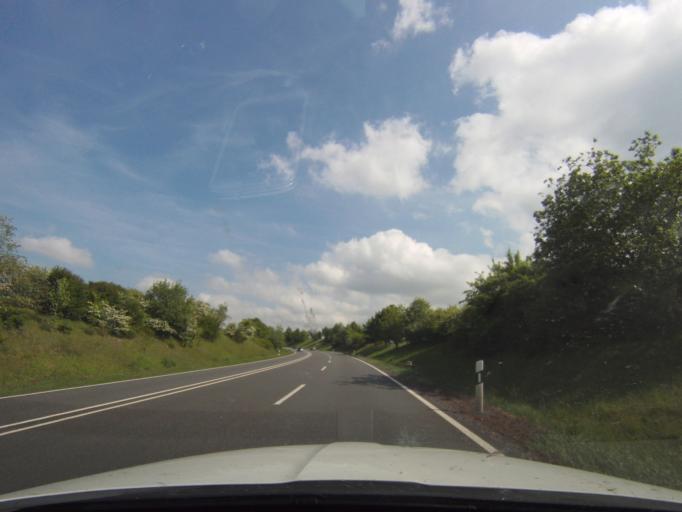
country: DE
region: Thuringia
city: Neustadt (Orla)
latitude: 50.7259
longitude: 11.7312
